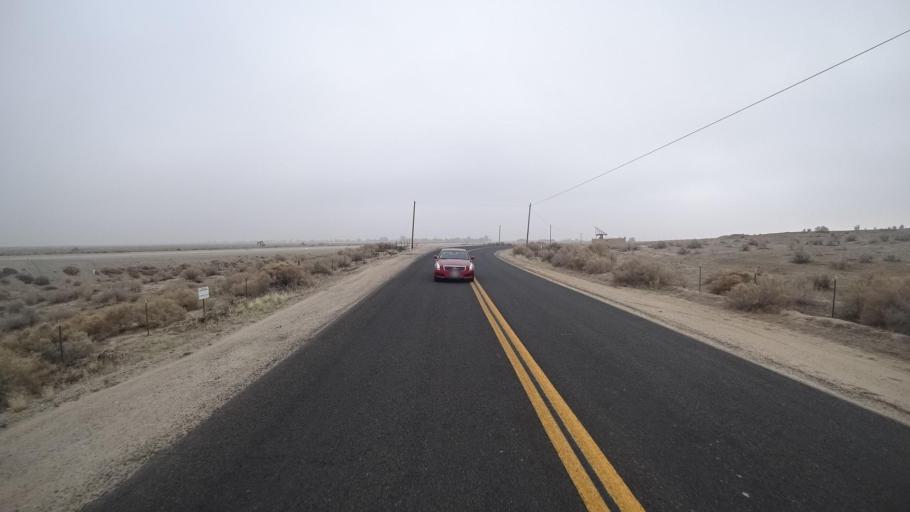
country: US
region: California
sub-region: Kern County
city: Ford City
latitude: 35.2490
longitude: -119.3032
